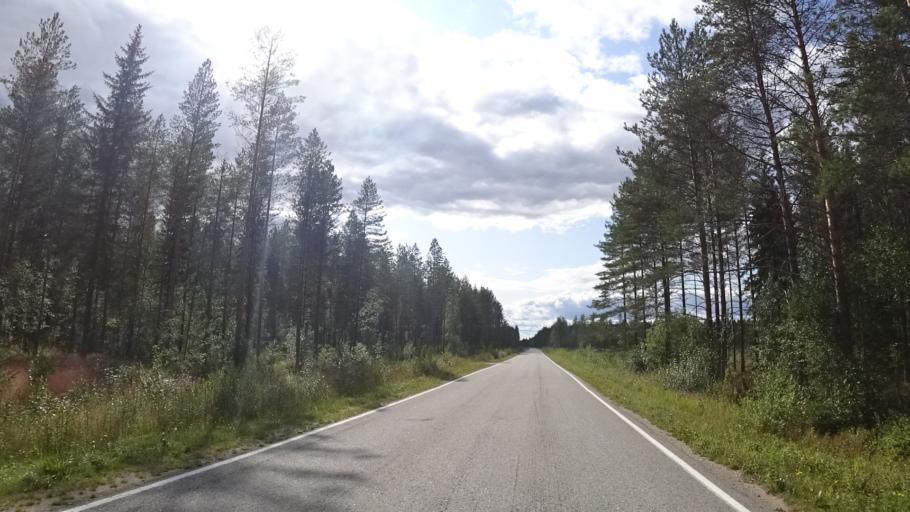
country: FI
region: North Karelia
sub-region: Joensuu
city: Ilomantsi
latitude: 62.4424
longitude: 31.0945
